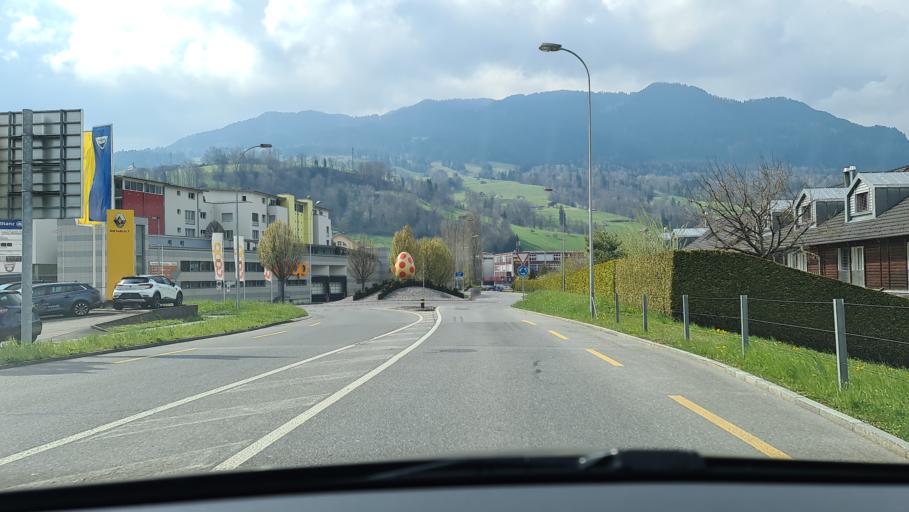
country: CH
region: Obwalden
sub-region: Obwalden
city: Sarnen
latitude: 46.8973
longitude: 8.2529
